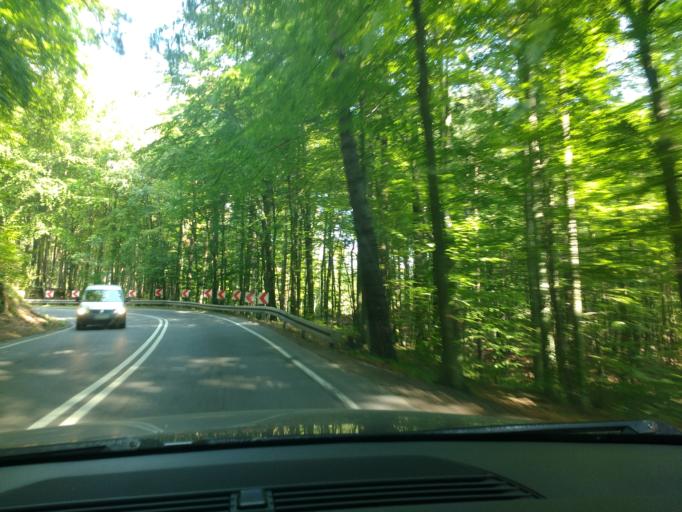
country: PL
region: Pomeranian Voivodeship
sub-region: Gdynia
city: Wielki Kack
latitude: 54.4593
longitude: 18.5080
